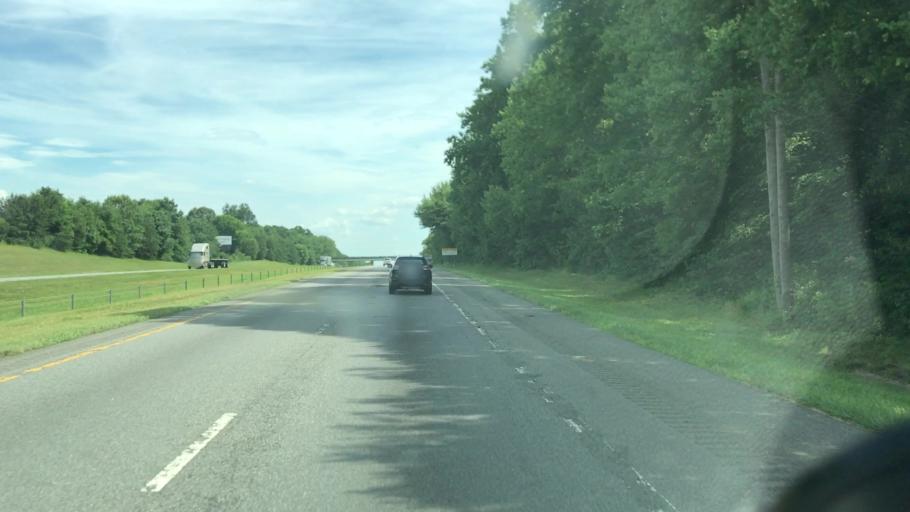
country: US
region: North Carolina
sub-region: Iredell County
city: Statesville
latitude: 35.8732
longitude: -80.8660
